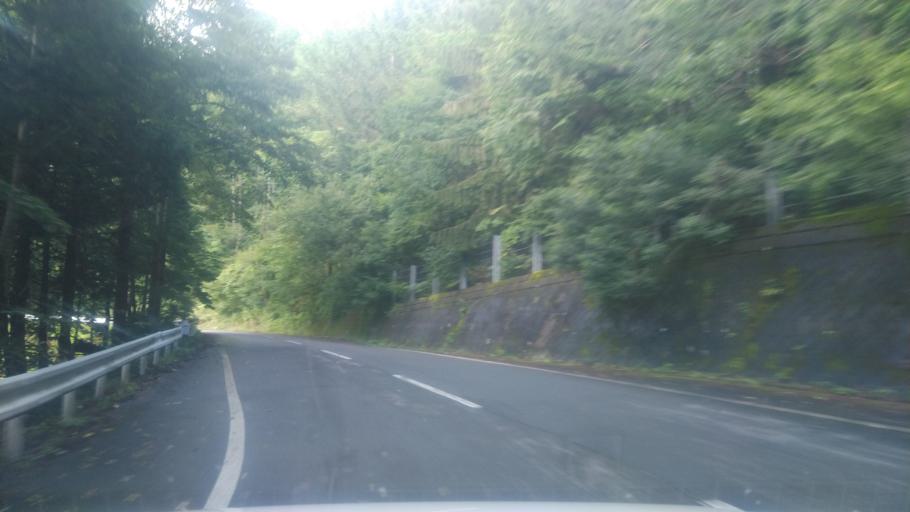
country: JP
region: Nagano
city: Ueda
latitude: 36.5127
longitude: 138.3659
